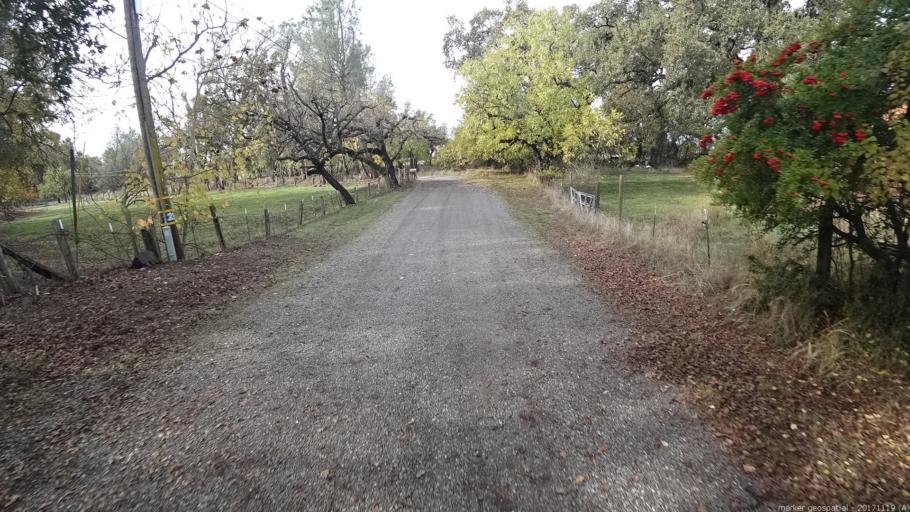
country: US
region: California
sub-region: Shasta County
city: Redding
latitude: 40.5144
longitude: -122.3521
